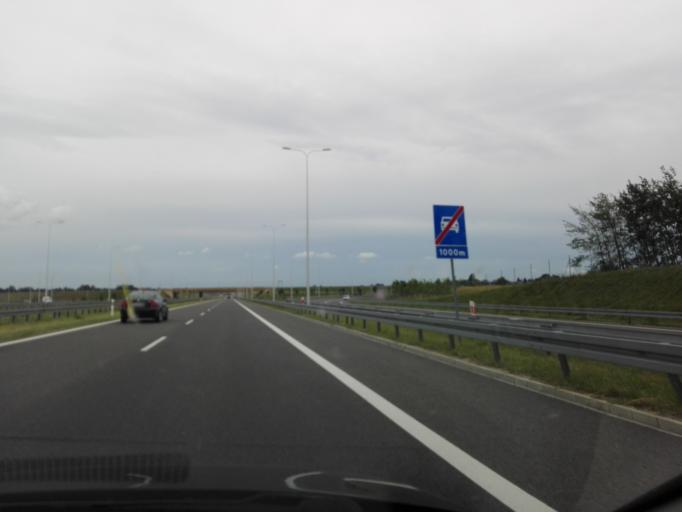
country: PL
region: Lublin Voivodeship
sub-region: Powiat lubelski
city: Jastkow
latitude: 51.2867
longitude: 22.4455
